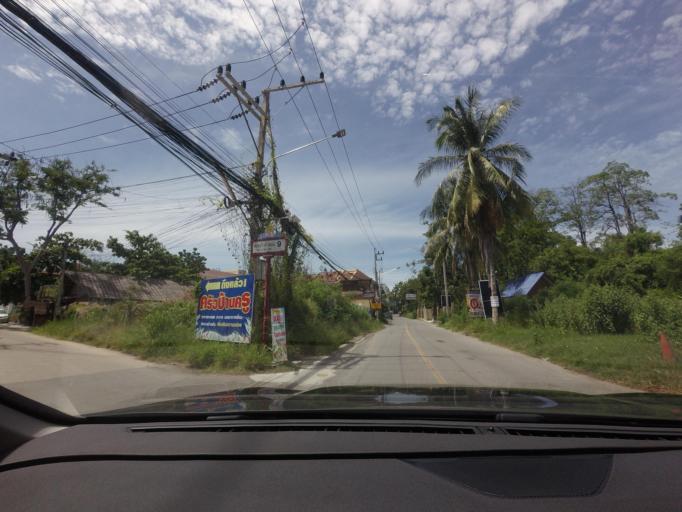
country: TH
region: Prachuap Khiri Khan
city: Hua Hin
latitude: 12.5131
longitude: 99.9760
